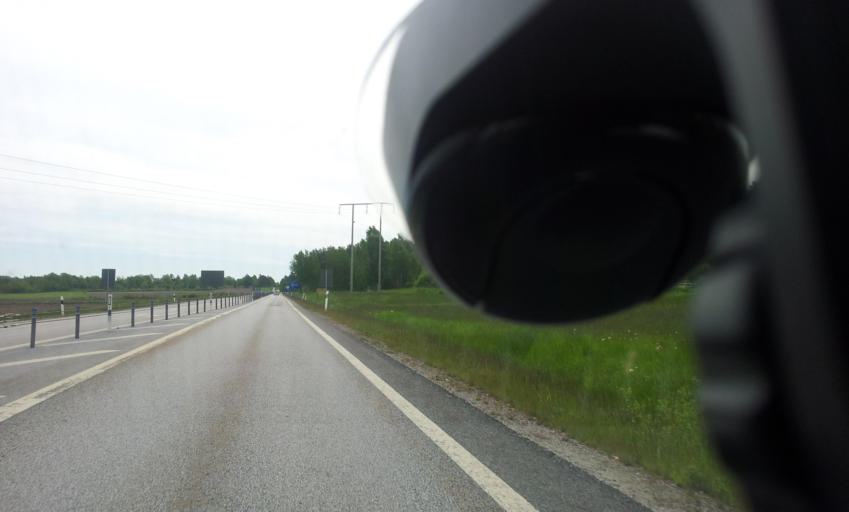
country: SE
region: Kalmar
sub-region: Vasterviks Kommun
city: Vaestervik
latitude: 57.7758
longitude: 16.5441
